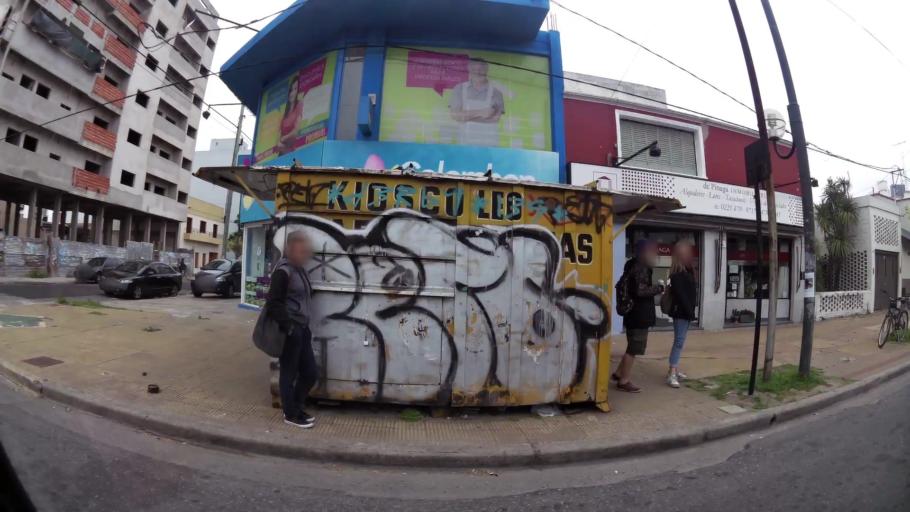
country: AR
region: Buenos Aires
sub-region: Partido de La Plata
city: La Plata
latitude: -34.9267
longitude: -57.9728
